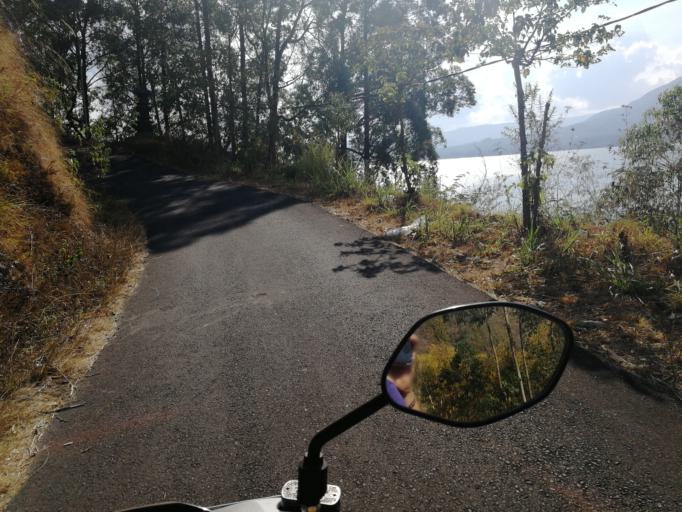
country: ID
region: Bali
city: Banjar Trunyan
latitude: -8.2553
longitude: 115.4247
